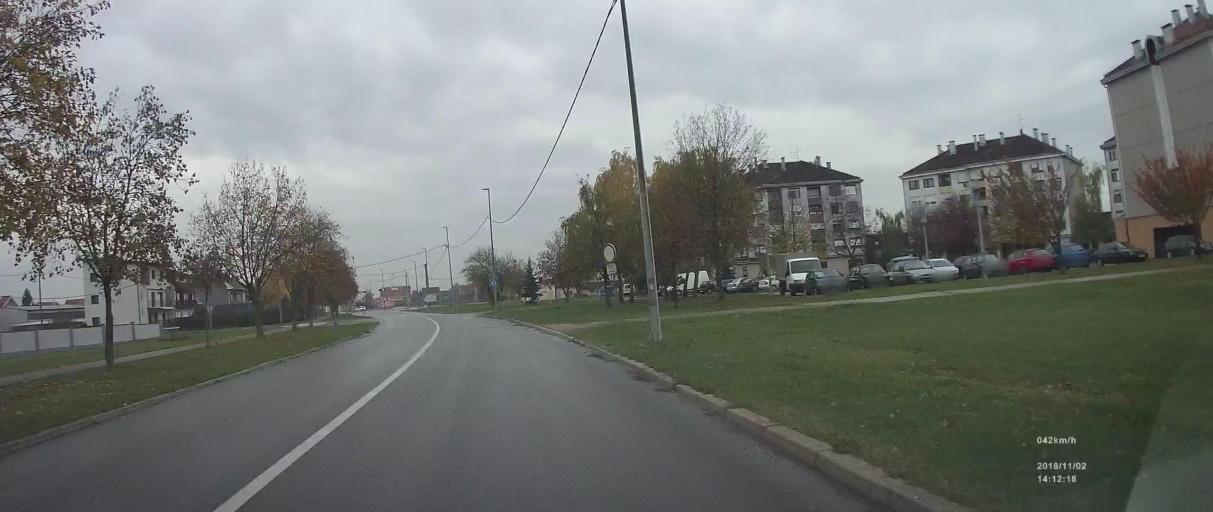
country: HR
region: Zagrebacka
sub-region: Grad Velika Gorica
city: Velika Gorica
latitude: 45.7054
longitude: 16.0638
